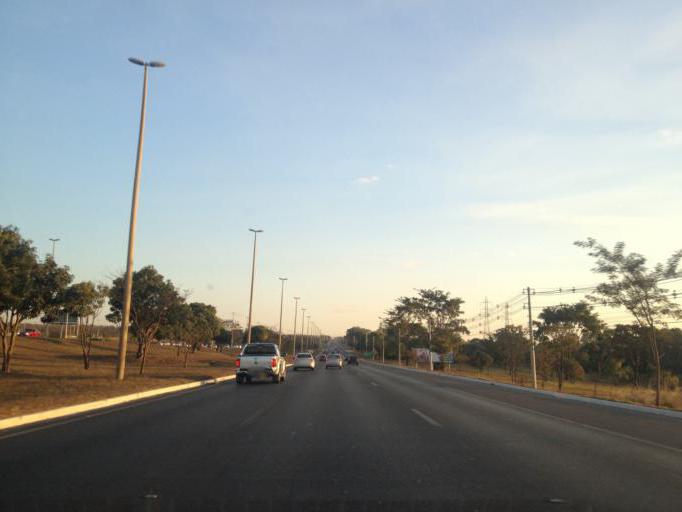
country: BR
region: Federal District
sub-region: Brasilia
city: Brasilia
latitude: -15.7362
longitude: -47.9148
